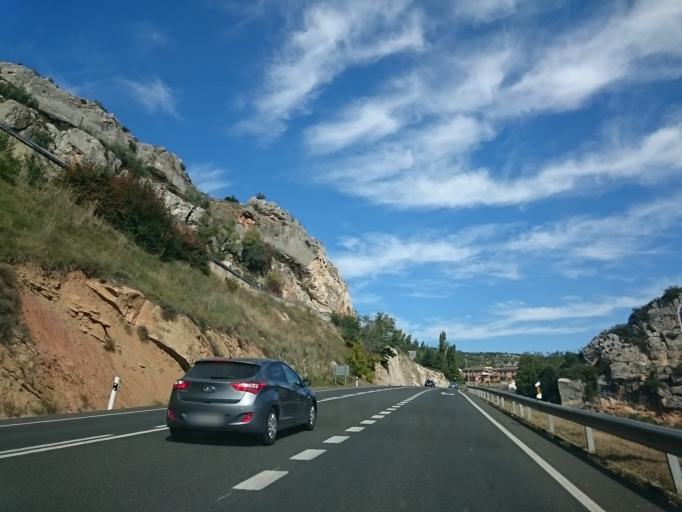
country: ES
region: Aragon
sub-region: Provincia de Huesca
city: Benavarri / Benabarre
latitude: 42.1062
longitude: 0.4846
